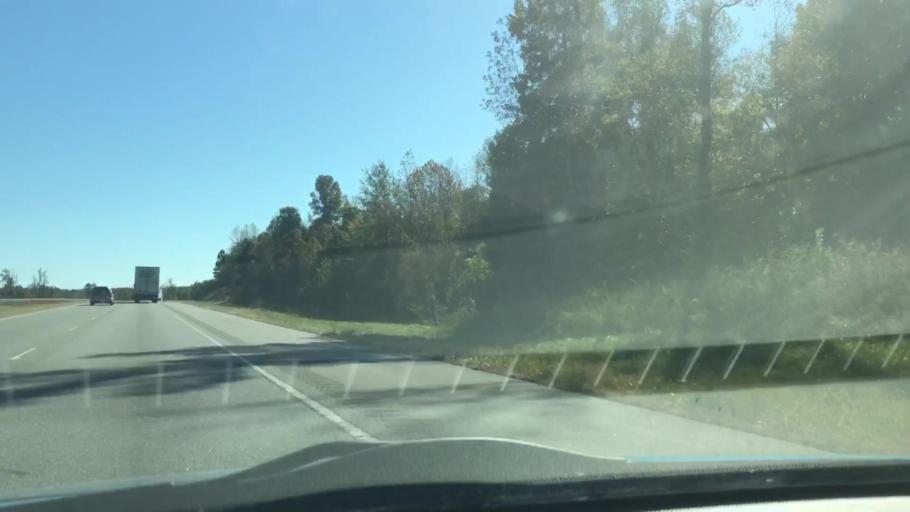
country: US
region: North Carolina
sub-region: Randolph County
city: Archdale
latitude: 35.9031
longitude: -79.9121
